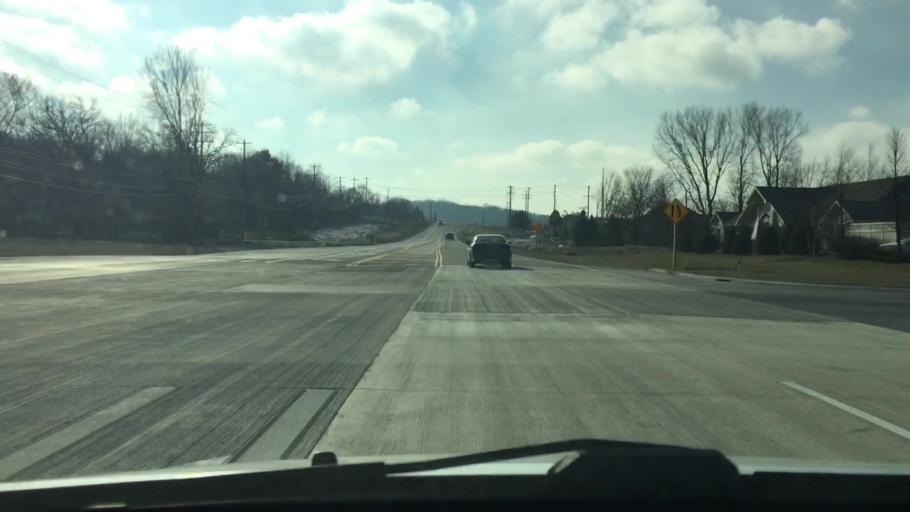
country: US
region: Wisconsin
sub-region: Waukesha County
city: Waukesha
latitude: 43.0186
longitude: -88.2860
